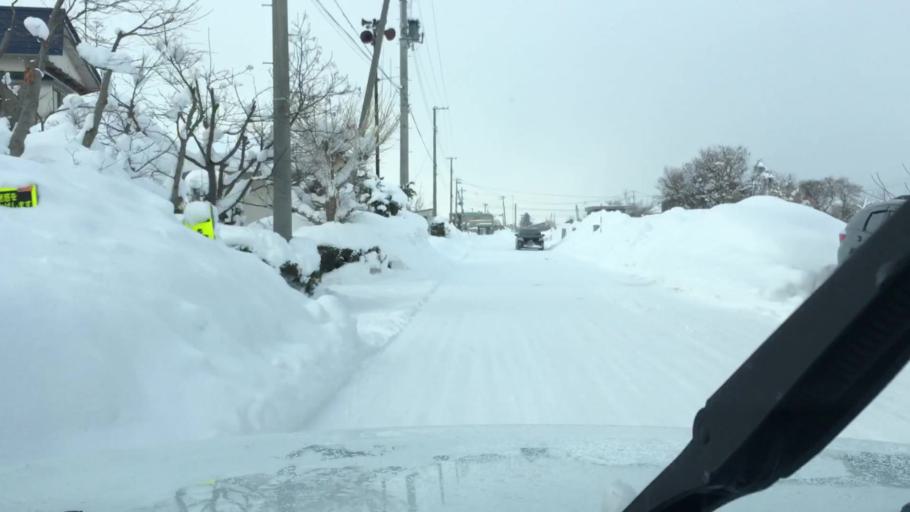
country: JP
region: Aomori
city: Hirosaki
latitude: 40.6540
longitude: 140.4800
